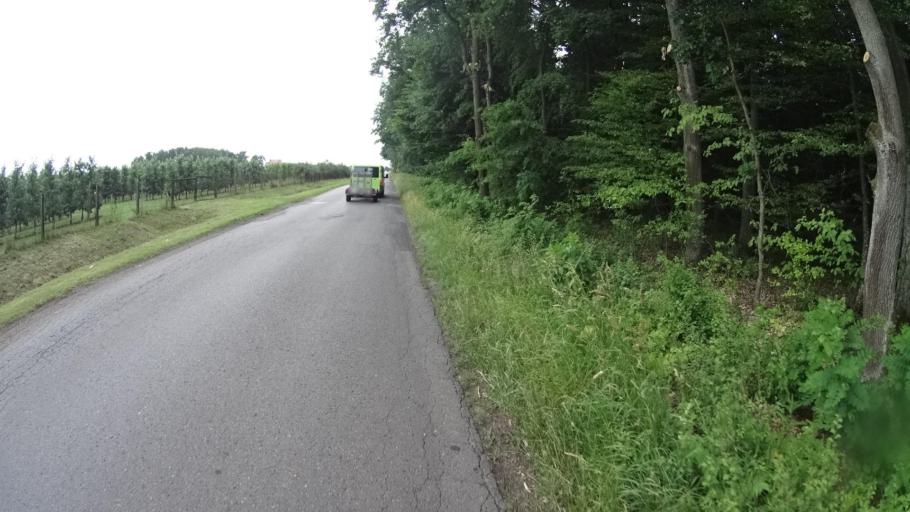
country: PL
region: Masovian Voivodeship
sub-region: Powiat grojecki
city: Goszczyn
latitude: 51.7785
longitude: 20.8535
